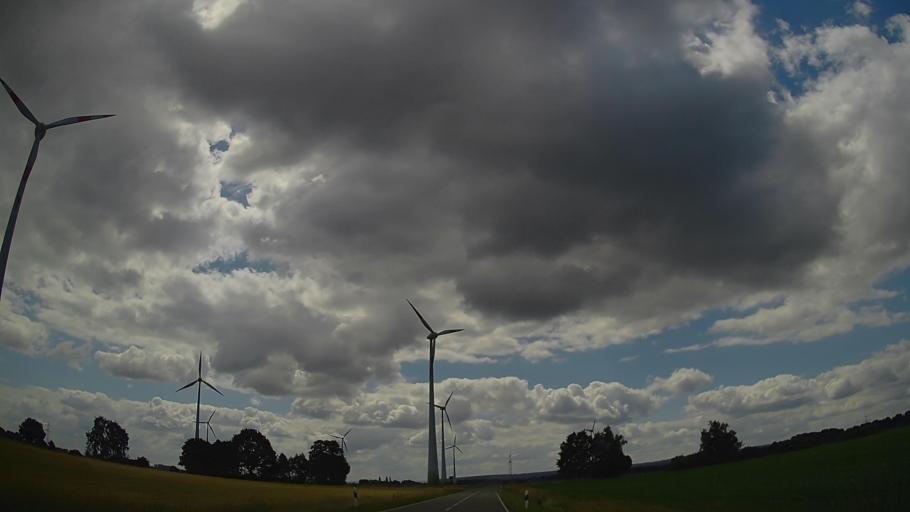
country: DE
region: Lower Saxony
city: Brockum
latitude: 52.5149
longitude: 8.4209
